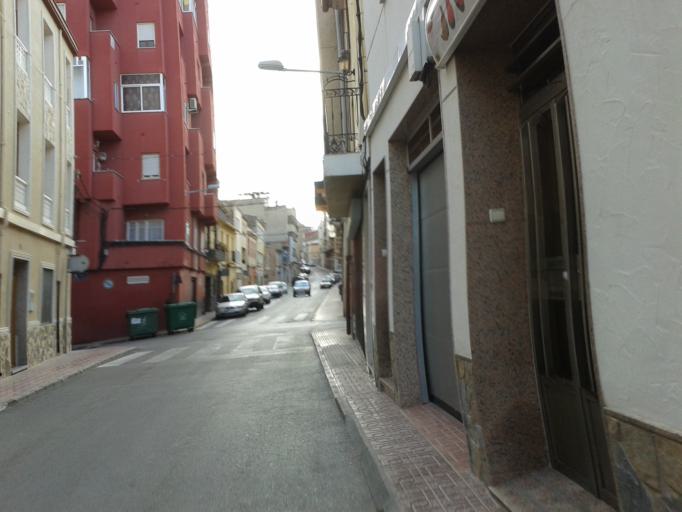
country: ES
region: Castille-La Mancha
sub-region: Provincia de Albacete
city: Caudete
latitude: 38.7070
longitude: -0.9883
